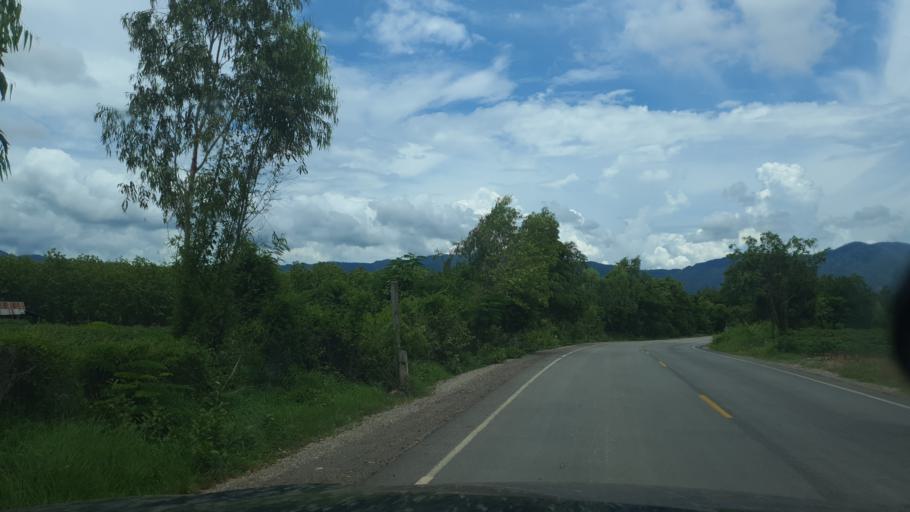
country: TH
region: Lampang
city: Sop Prap
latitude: 17.9224
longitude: 99.3840
